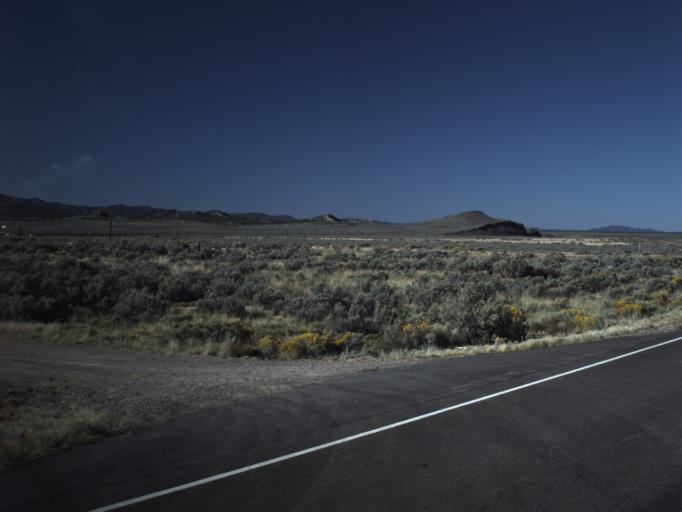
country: US
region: Utah
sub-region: Washington County
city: Enterprise
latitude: 37.8028
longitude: -113.9243
